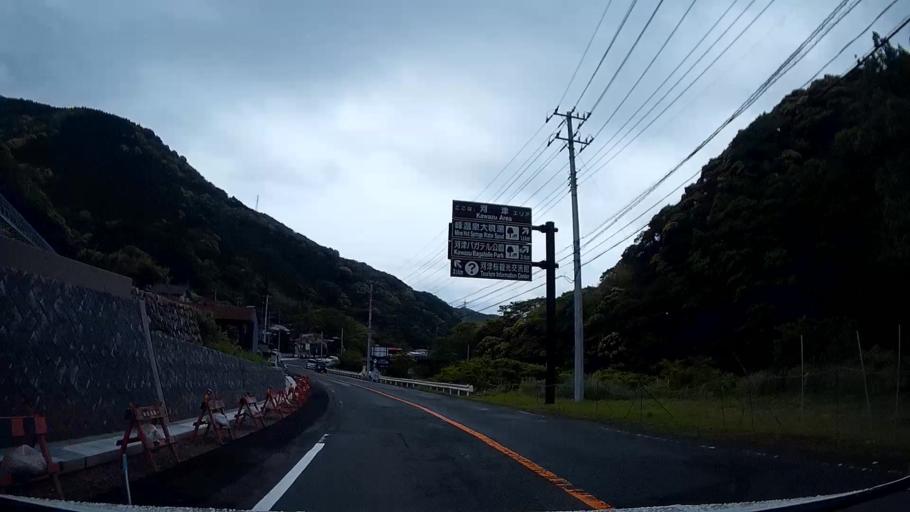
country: JP
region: Shizuoka
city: Shimoda
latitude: 34.7692
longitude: 138.9713
